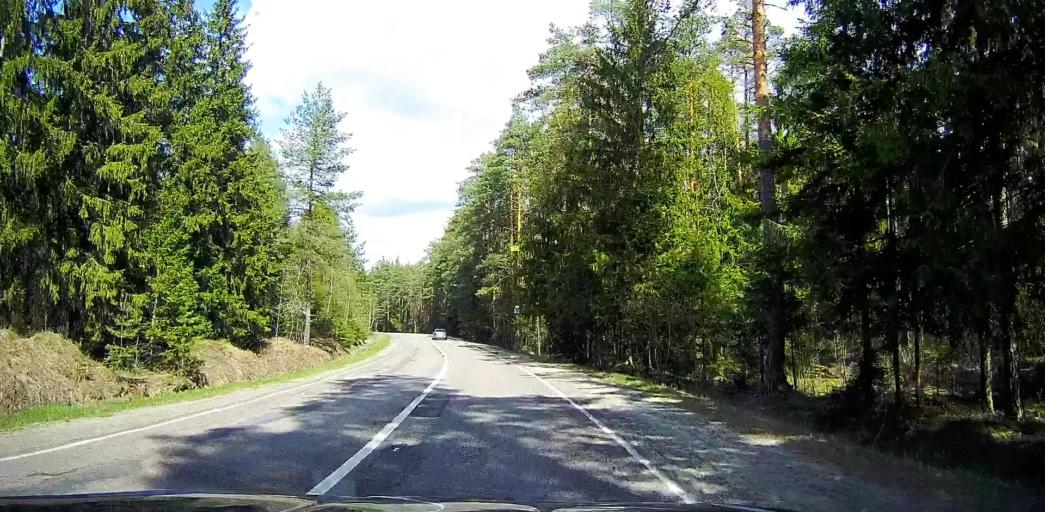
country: RU
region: Moskovskaya
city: Davydovo
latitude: 55.5664
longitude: 38.8205
